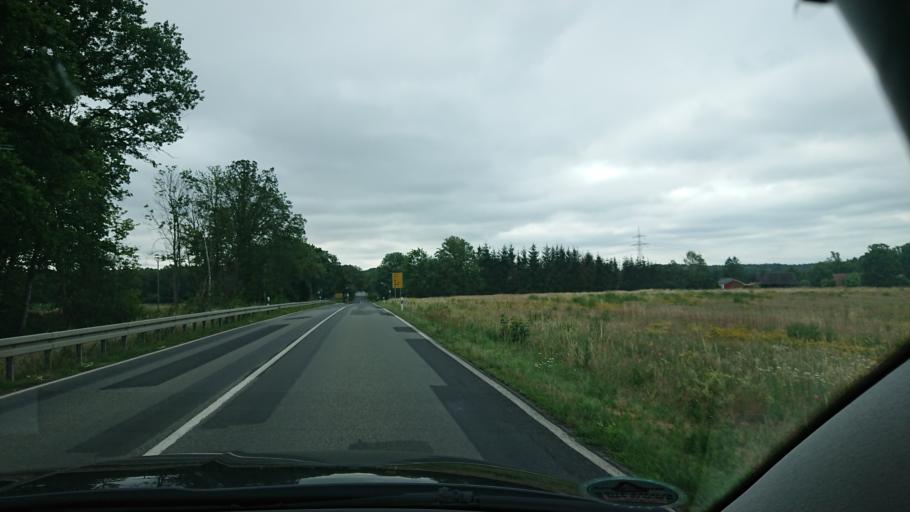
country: DE
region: Brandenburg
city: Bad Wilsnack
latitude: 53.0322
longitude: 11.9690
